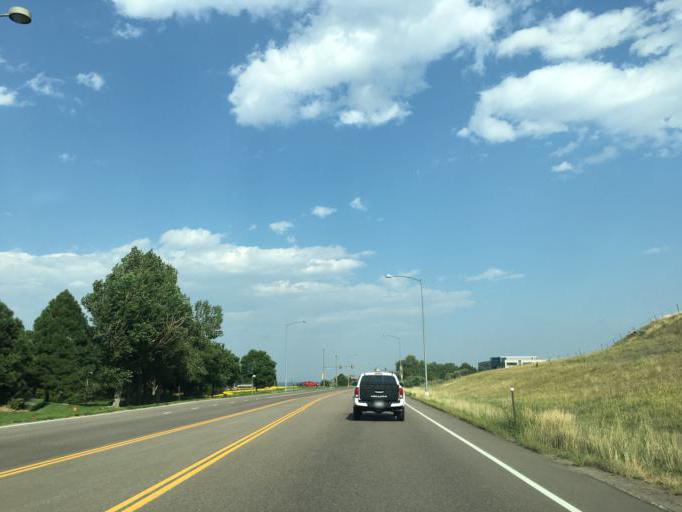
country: US
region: Colorado
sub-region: Broomfield County
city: Broomfield
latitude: 39.9166
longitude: -105.1137
